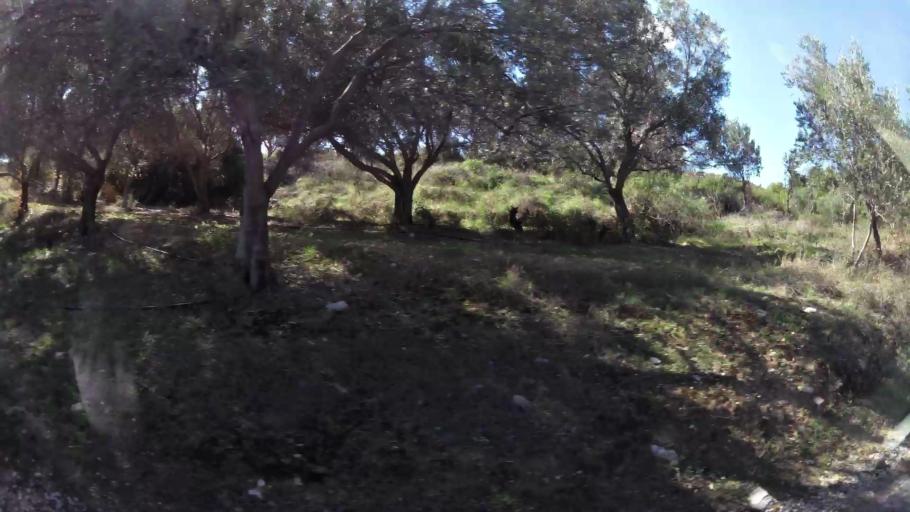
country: GR
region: Attica
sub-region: Nomarchia Anatolikis Attikis
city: Dioni
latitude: 38.0170
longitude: 23.9281
